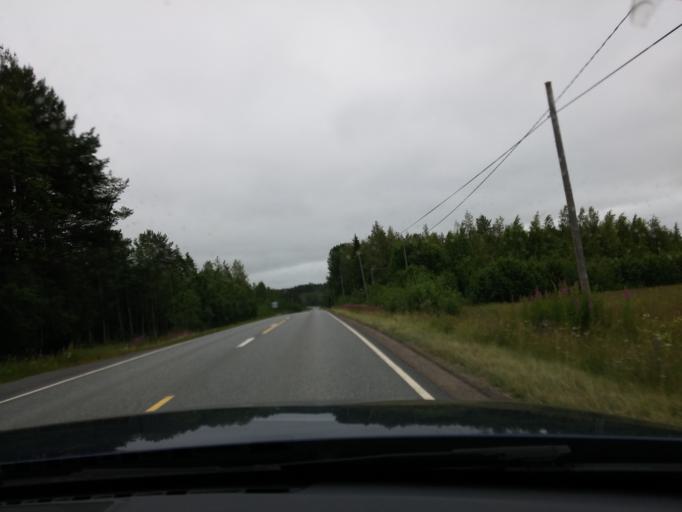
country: FI
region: Central Finland
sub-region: Joutsa
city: Joutsa
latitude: 61.7855
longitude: 26.0438
